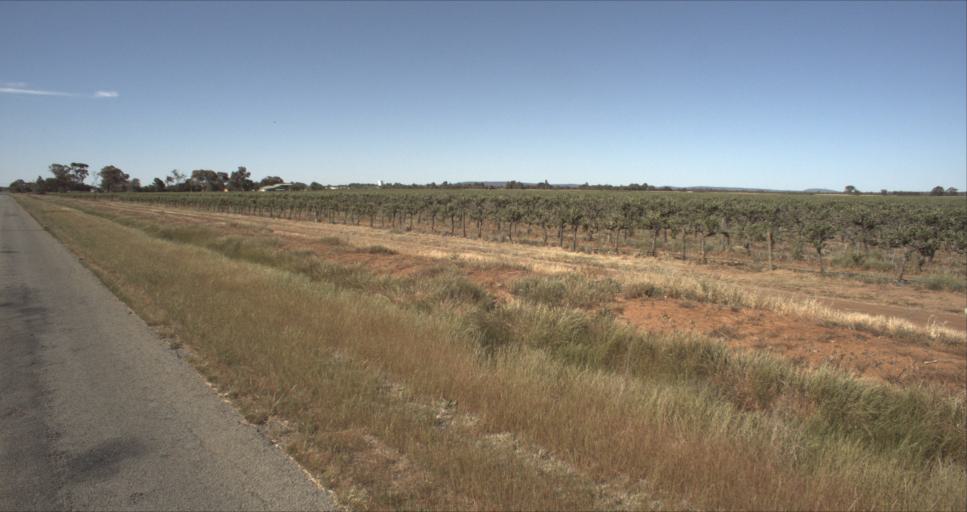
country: AU
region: New South Wales
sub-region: Leeton
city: Leeton
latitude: -34.5768
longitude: 146.3806
